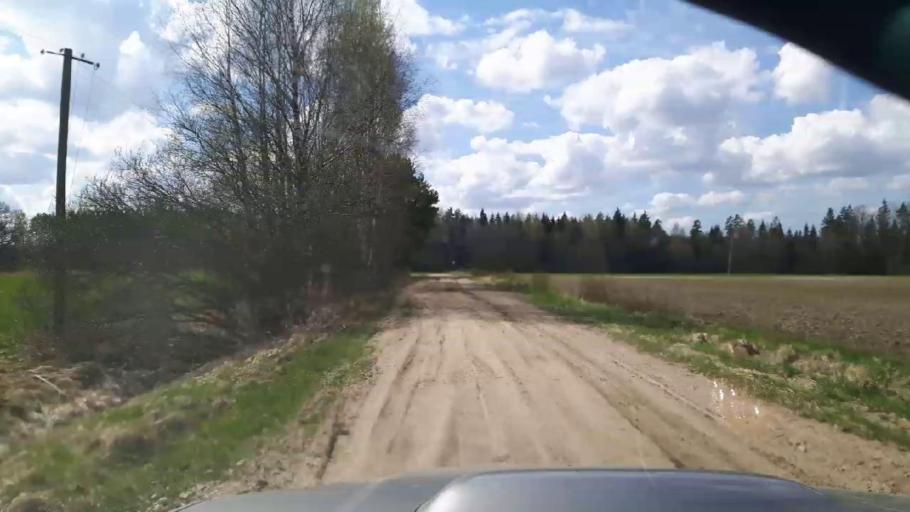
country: EE
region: Paernumaa
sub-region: Vaendra vald (alev)
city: Vandra
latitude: 58.5372
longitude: 25.0666
